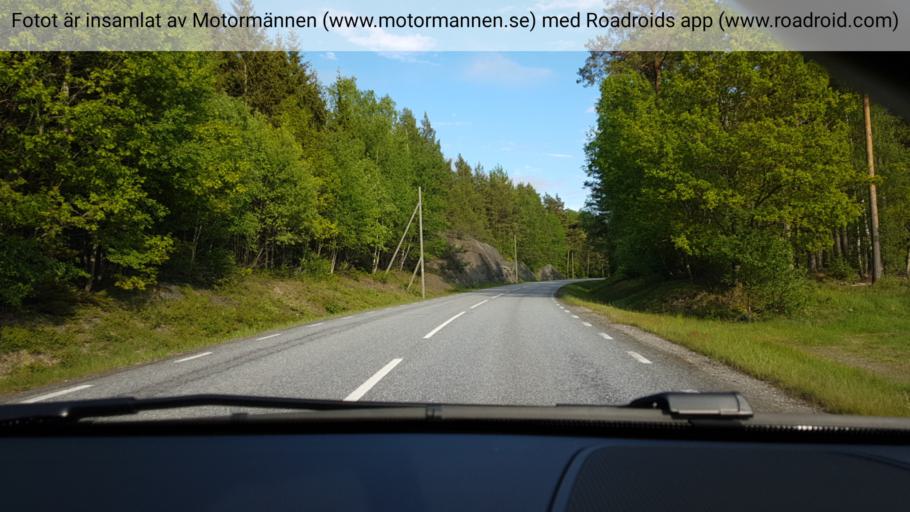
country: SE
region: Stockholm
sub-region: Nynashamns Kommun
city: Osmo
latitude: 58.9671
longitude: 17.9564
